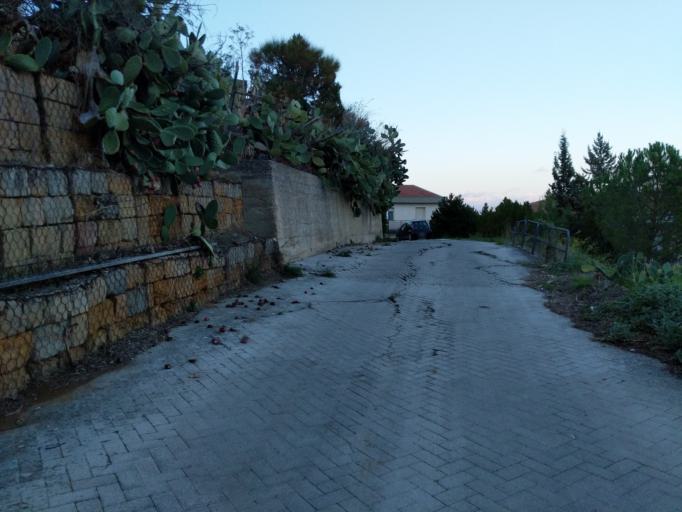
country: IT
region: Sicily
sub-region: Provincia di Caltanissetta
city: Sutera
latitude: 37.5249
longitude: 13.7375
